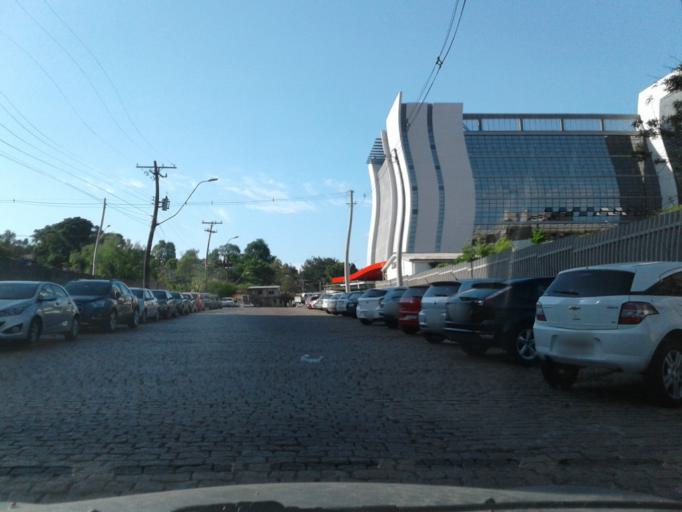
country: BR
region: Rio Grande do Sul
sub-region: Porto Alegre
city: Porto Alegre
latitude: -30.0527
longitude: -51.1595
